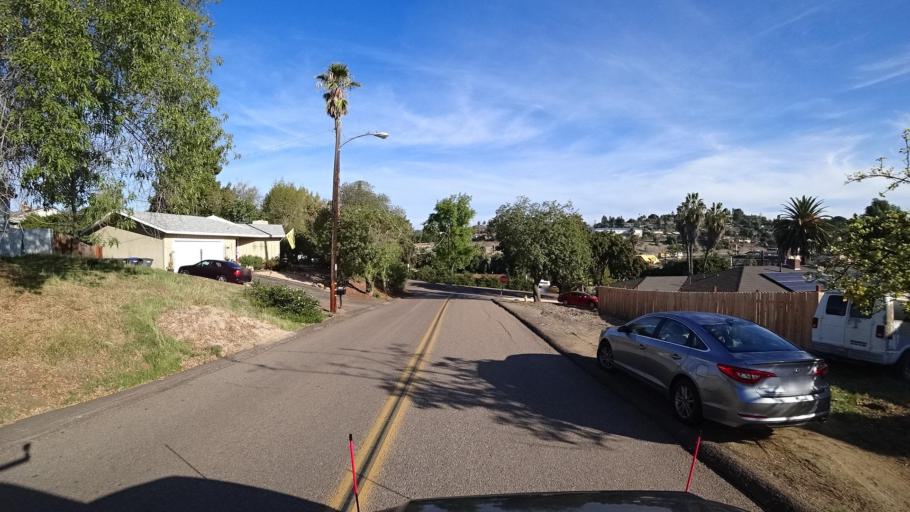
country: US
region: California
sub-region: San Diego County
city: Casa de Oro-Mount Helix
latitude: 32.7419
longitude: -116.9735
